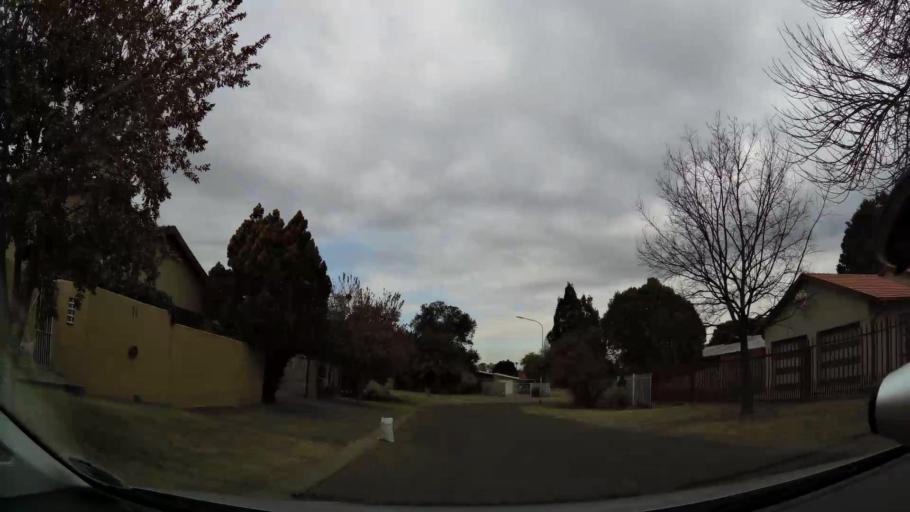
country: ZA
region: Orange Free State
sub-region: Fezile Dabi District Municipality
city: Kroonstad
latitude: -27.6519
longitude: 27.2461
